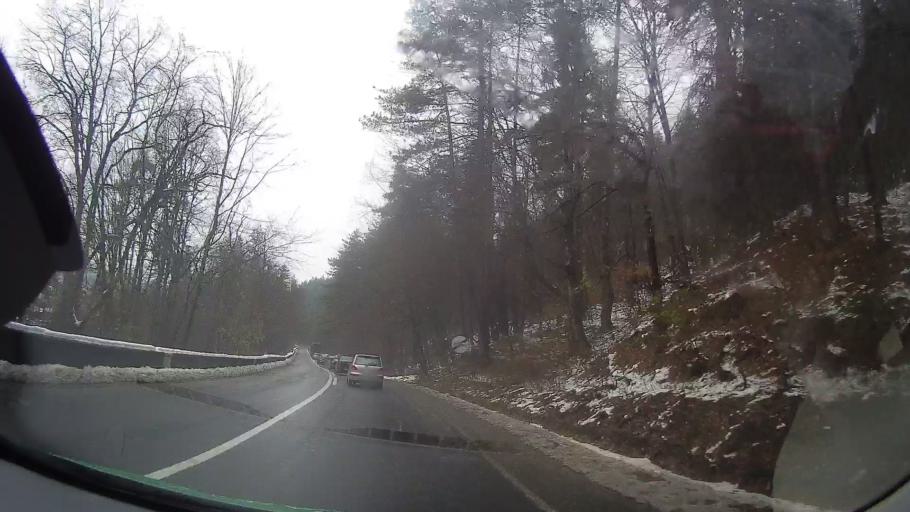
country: RO
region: Neamt
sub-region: Comuna Tarcau
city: Tarcau
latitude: 46.8954
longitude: 26.1230
